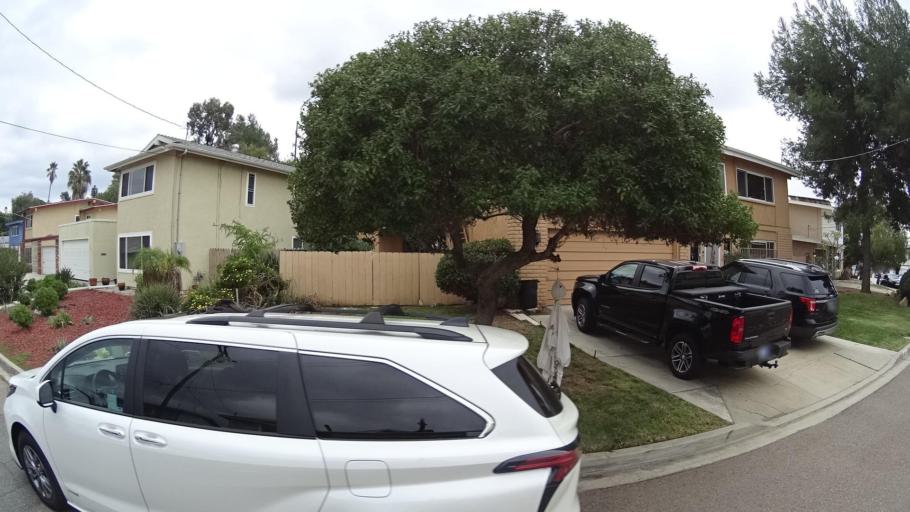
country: US
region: California
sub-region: San Diego County
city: Spring Valley
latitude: 32.7504
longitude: -117.0108
